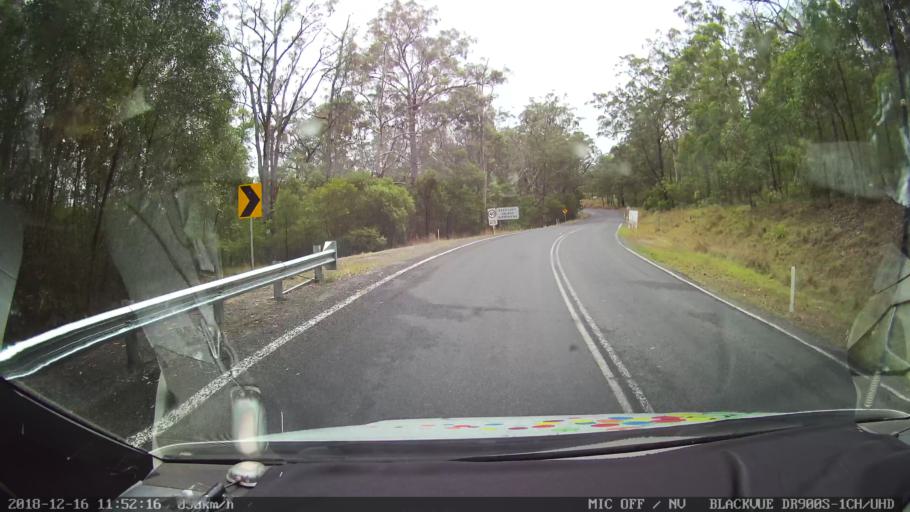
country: AU
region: New South Wales
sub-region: Tenterfield Municipality
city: Carrolls Creek
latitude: -28.9035
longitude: 152.2710
